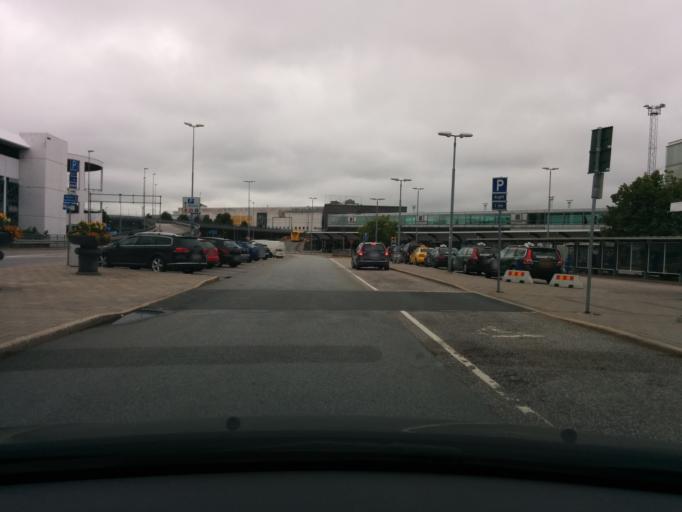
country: SE
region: Stockholm
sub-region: Sigtuna Kommun
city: Marsta
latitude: 59.6478
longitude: 17.9292
